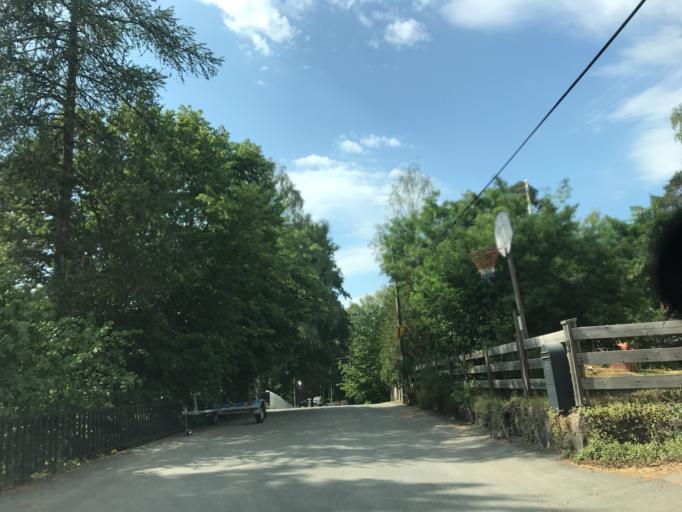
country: SE
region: Stockholm
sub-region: Stockholms Kommun
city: Kista
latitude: 59.4088
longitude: 17.9705
